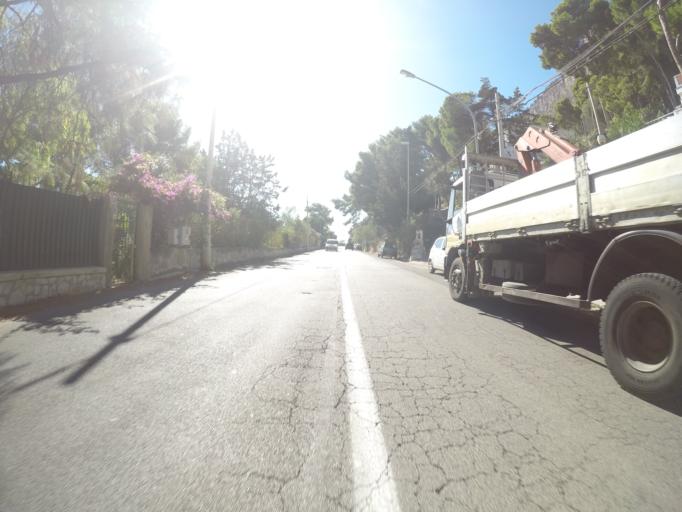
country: IT
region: Sicily
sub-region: Palermo
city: Palermo
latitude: 38.1816
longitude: 13.3652
